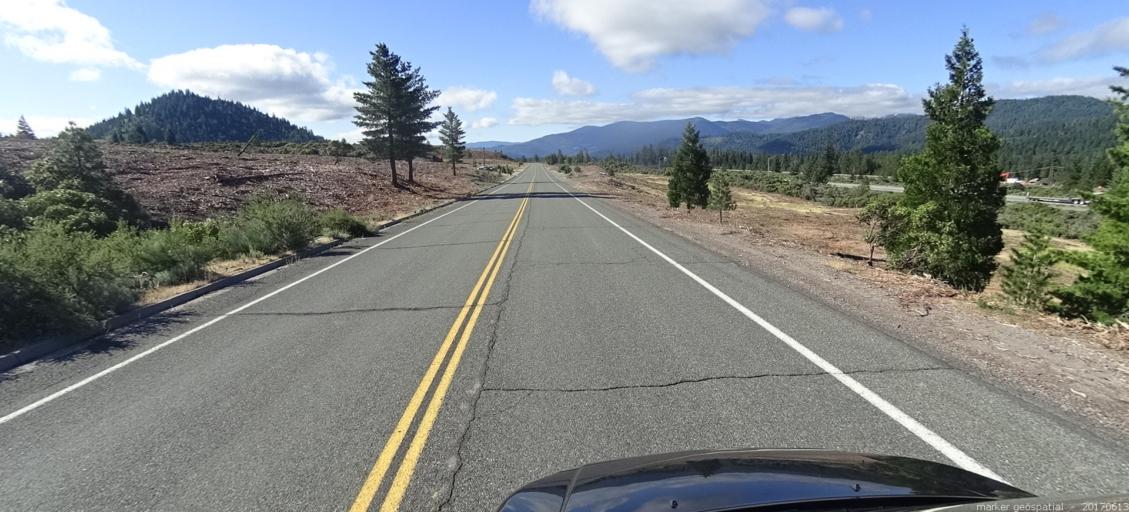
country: US
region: California
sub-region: Siskiyou County
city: Mount Shasta
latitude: 41.3435
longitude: -122.3399
